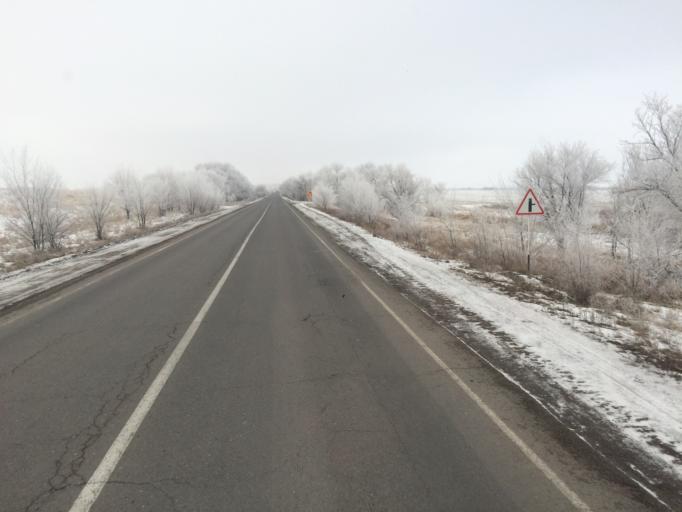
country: KG
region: Chuy
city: Bystrovka
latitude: 43.3232
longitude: 75.9220
